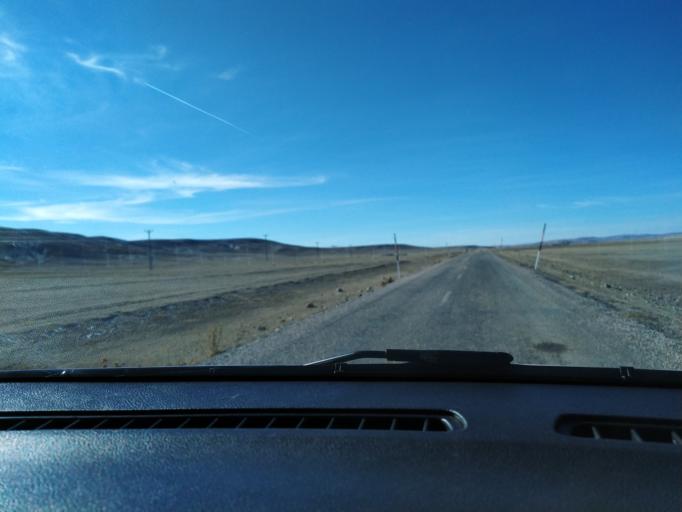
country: TR
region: Kayseri
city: Orensehir
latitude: 39.0974
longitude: 36.6959
